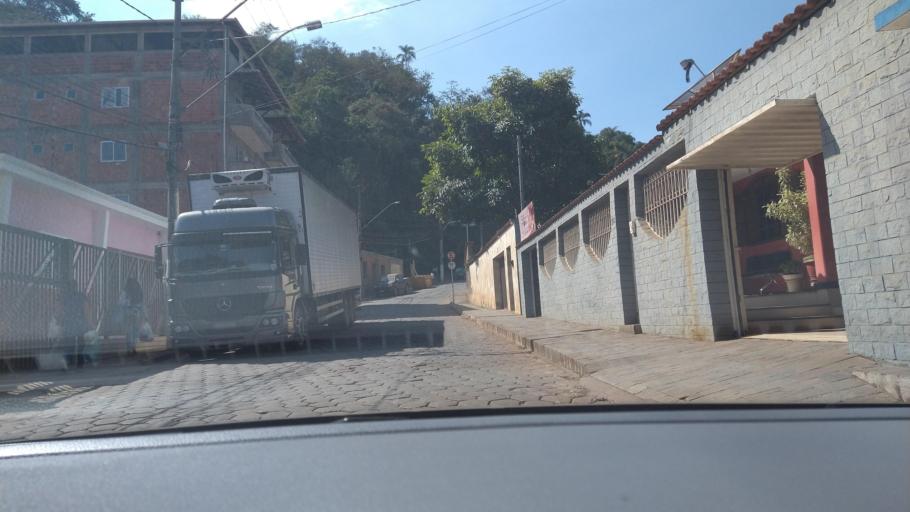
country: BR
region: Minas Gerais
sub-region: Rio Piracicaba
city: Rio Piracicaba
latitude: -19.9288
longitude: -43.1729
